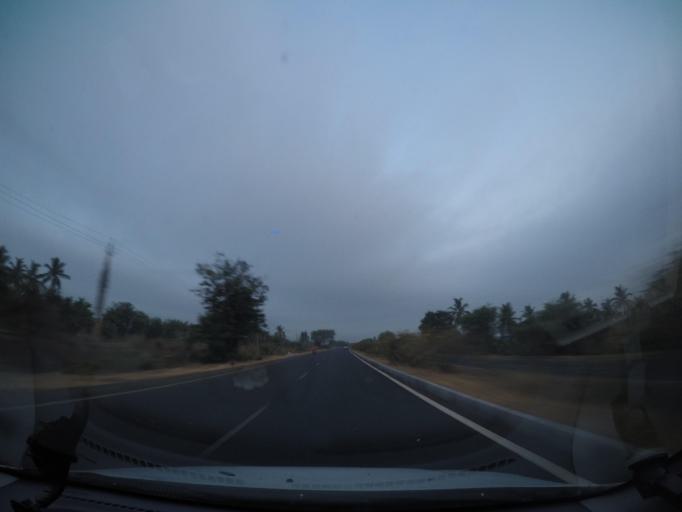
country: IN
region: Andhra Pradesh
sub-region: West Godavari
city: Tadepallegudem
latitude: 16.8099
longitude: 81.3616
